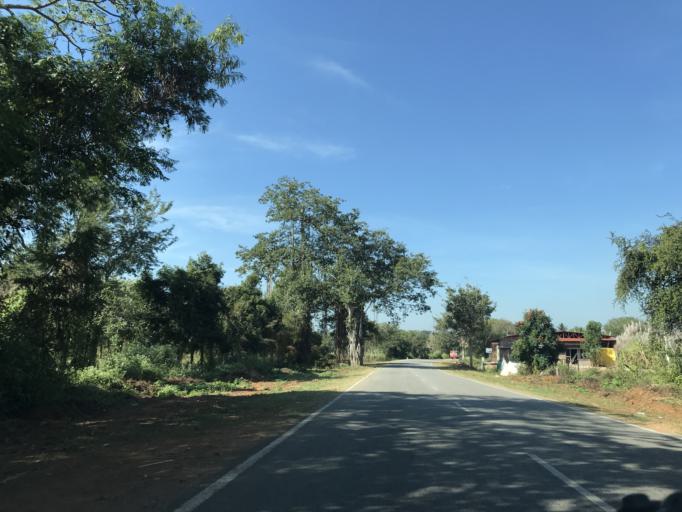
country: IN
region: Karnataka
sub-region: Mysore
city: Sargur
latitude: 12.1309
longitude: 76.5027
